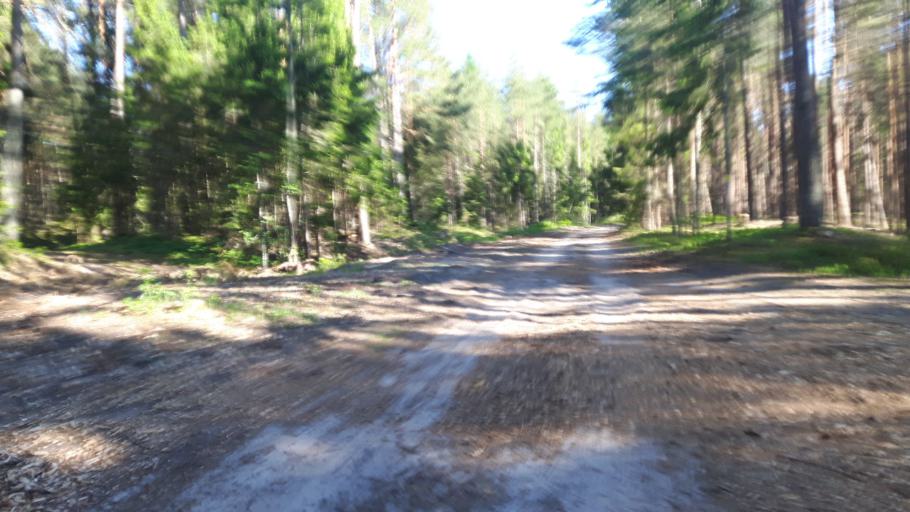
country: LV
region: Salacgrivas
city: Salacgriva
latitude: 57.7173
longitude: 24.3479
